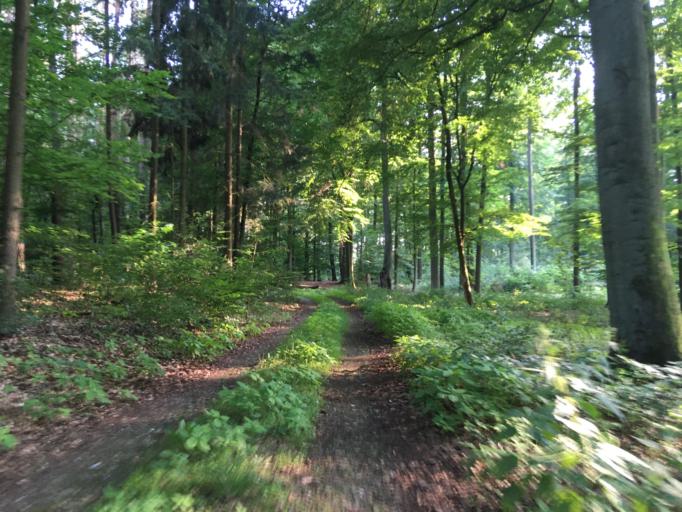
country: DE
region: Brandenburg
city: Wandlitz
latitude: 52.7207
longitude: 13.5260
